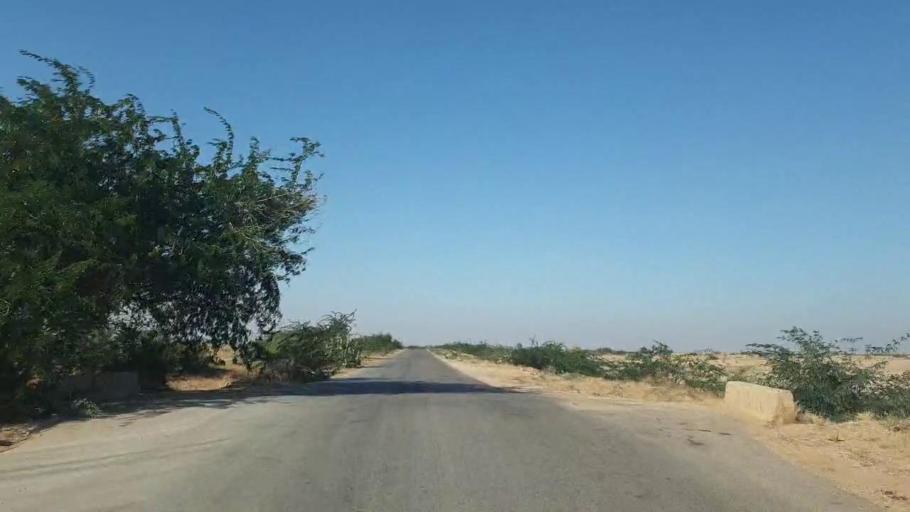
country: PK
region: Sindh
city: Malir Cantonment
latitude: 25.2574
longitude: 67.6012
